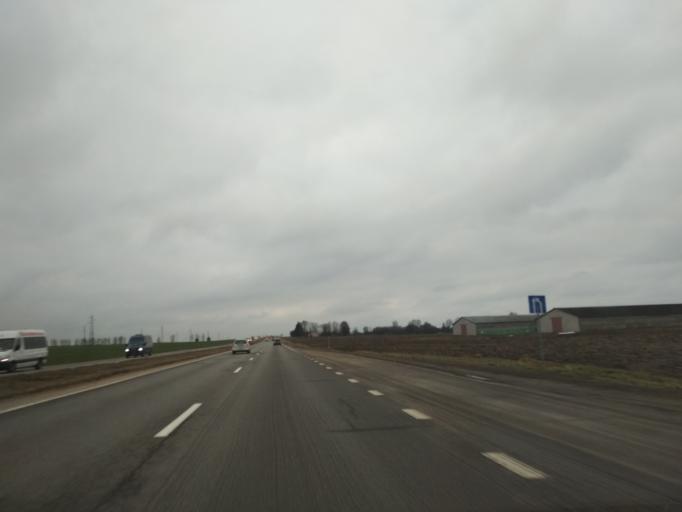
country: BY
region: Minsk
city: Mar''ina Horka
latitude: 53.5931
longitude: 28.0979
